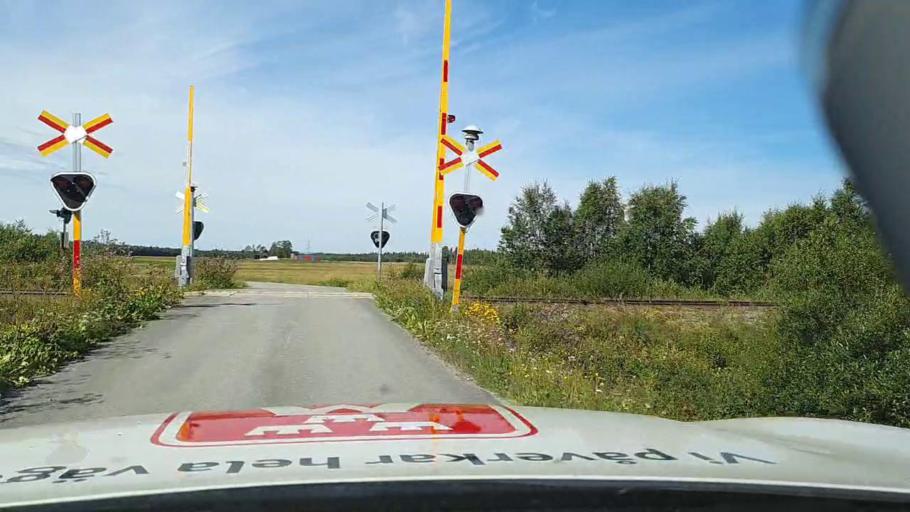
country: SE
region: Jaemtland
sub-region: Stroemsunds Kommun
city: Stroemsund
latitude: 63.6942
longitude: 15.3781
